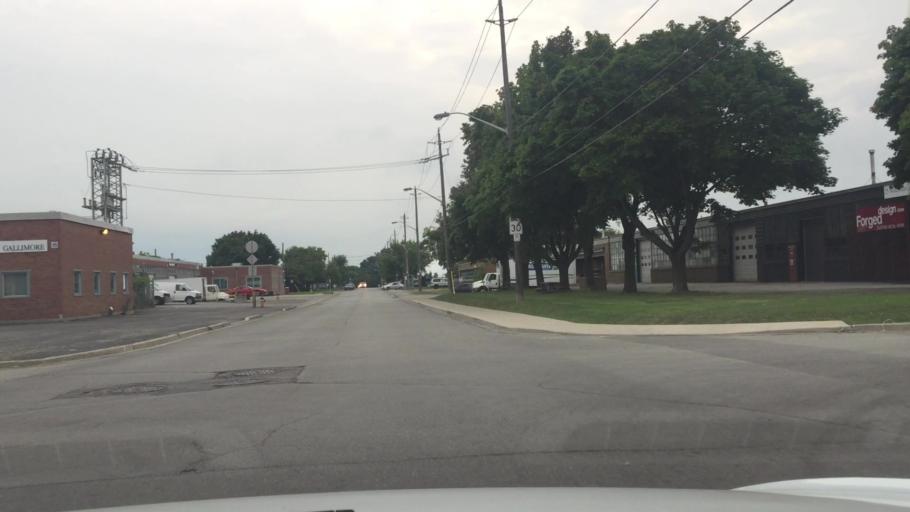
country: CA
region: Ontario
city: Scarborough
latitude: 43.7129
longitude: -79.3144
